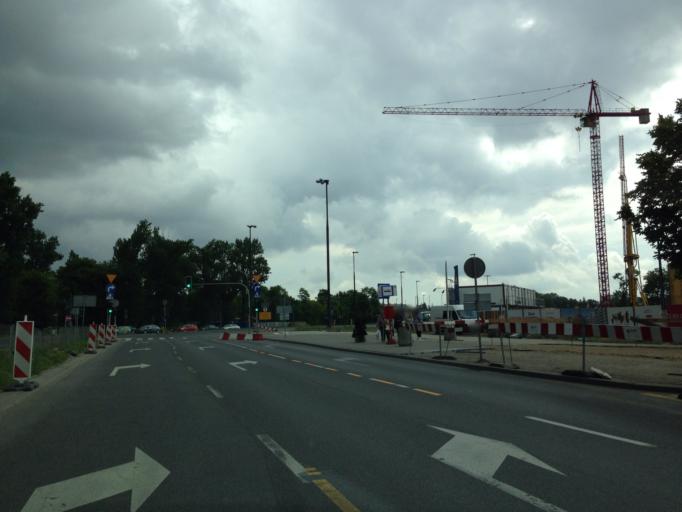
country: PL
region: Masovian Voivodeship
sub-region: Warszawa
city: Zoliborz
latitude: 52.2754
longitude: 20.9625
